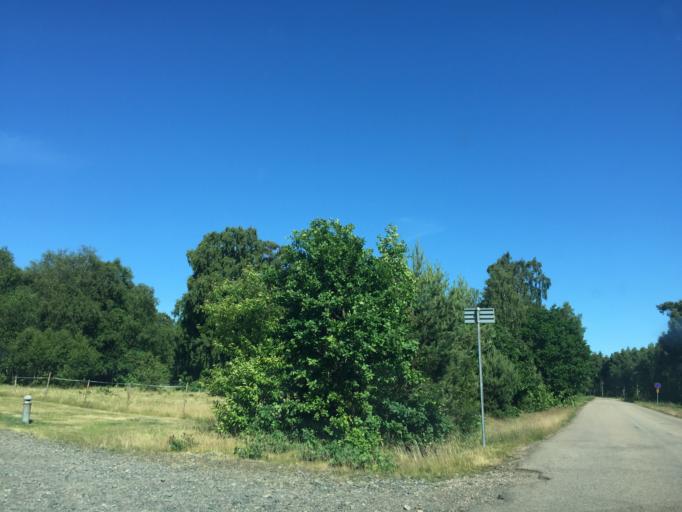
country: SE
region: Skane
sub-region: Angelholms Kommun
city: AEngelholm
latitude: 56.2315
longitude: 12.8323
